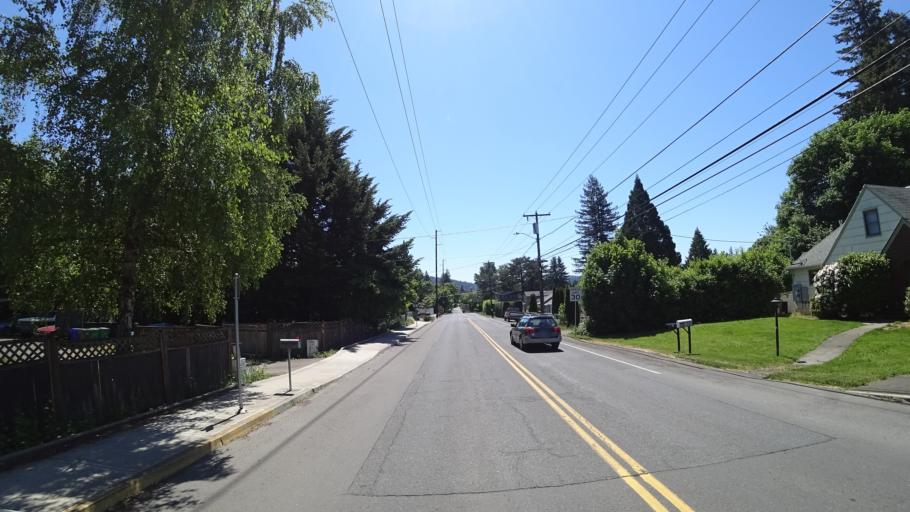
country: US
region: Oregon
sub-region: Clackamas County
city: Happy Valley
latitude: 45.4834
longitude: -122.5236
